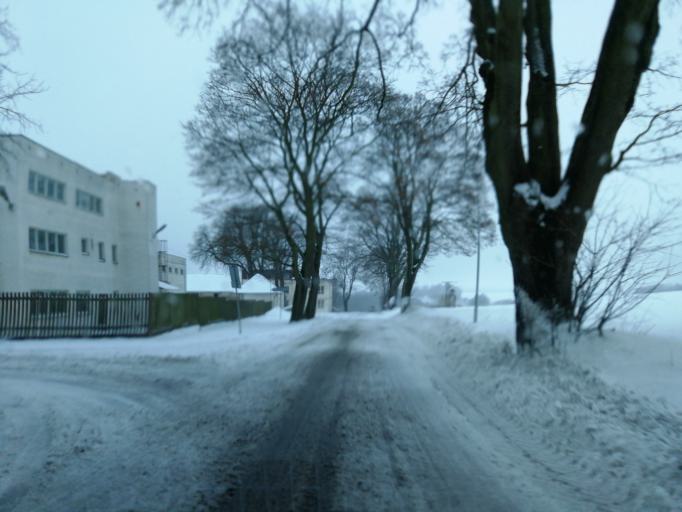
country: CZ
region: Vysocina
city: Heralec
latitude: 49.5322
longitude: 15.4524
